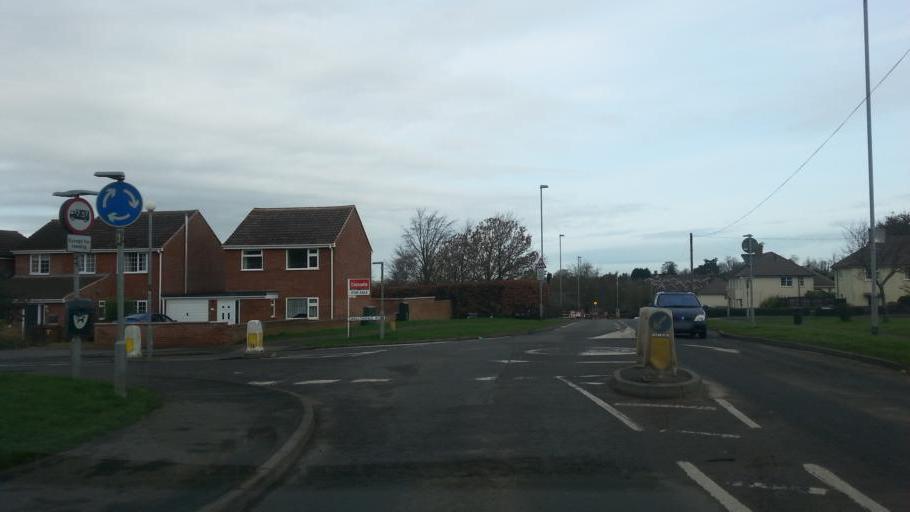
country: GB
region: England
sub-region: Leicestershire
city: Melton Mowbray
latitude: 52.7516
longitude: -0.8899
